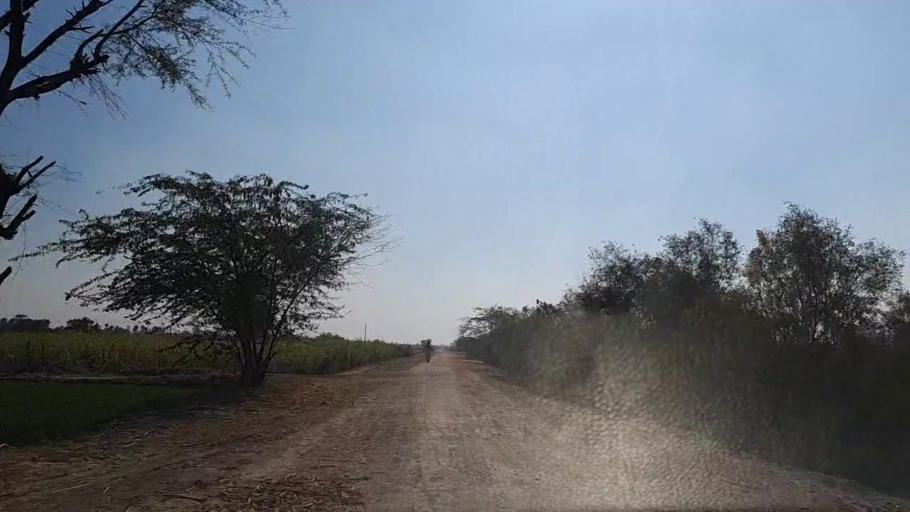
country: PK
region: Sindh
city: Bandhi
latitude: 26.5461
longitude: 68.3321
